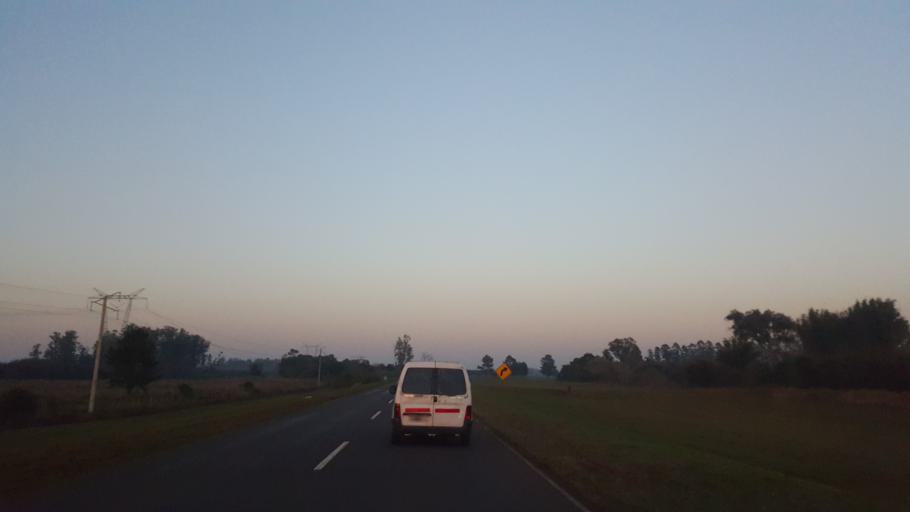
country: PY
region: Itapua
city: San Cosme y Damian
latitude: -27.6113
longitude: -56.3622
